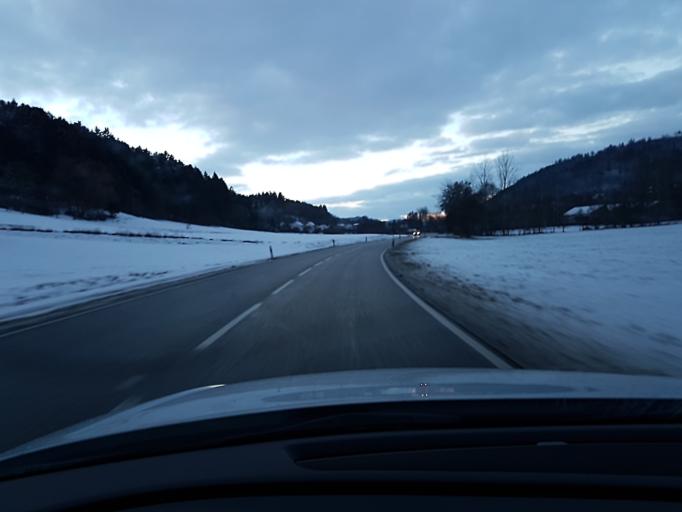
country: DE
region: Baden-Wuerttemberg
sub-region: Regierungsbezirk Stuttgart
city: Murrhardt
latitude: 48.9725
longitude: 9.6142
